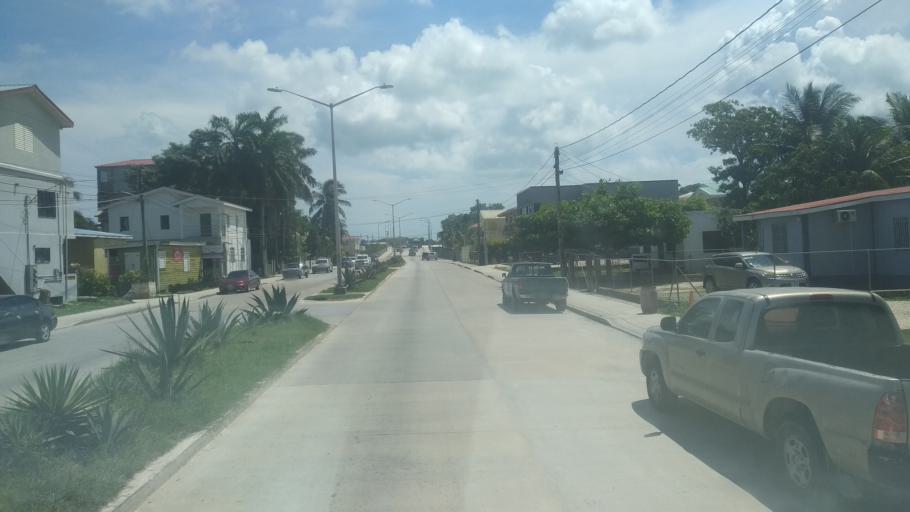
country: BZ
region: Belize
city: Belize City
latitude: 17.5101
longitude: -88.2215
